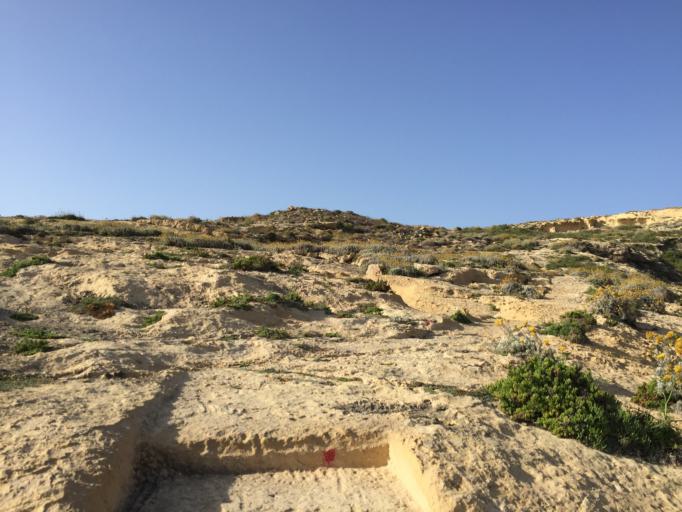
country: MT
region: Saint Lawrence
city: San Lawrenz
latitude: 36.0534
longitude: 14.1898
